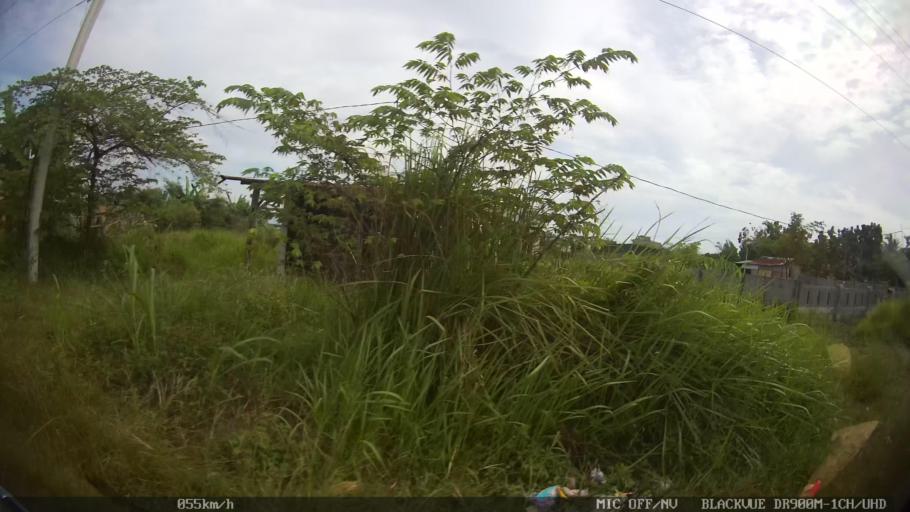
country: ID
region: North Sumatra
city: Percut
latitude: 3.6200
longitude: 98.7753
